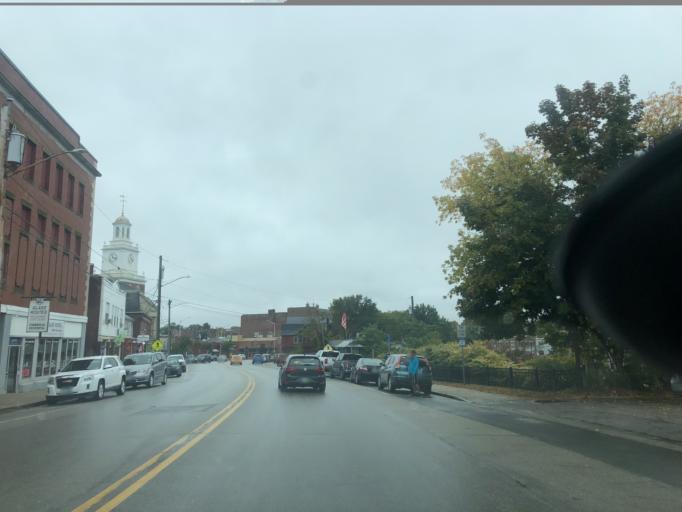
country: US
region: New Hampshire
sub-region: Strafford County
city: Dover
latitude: 43.1928
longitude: -70.8735
